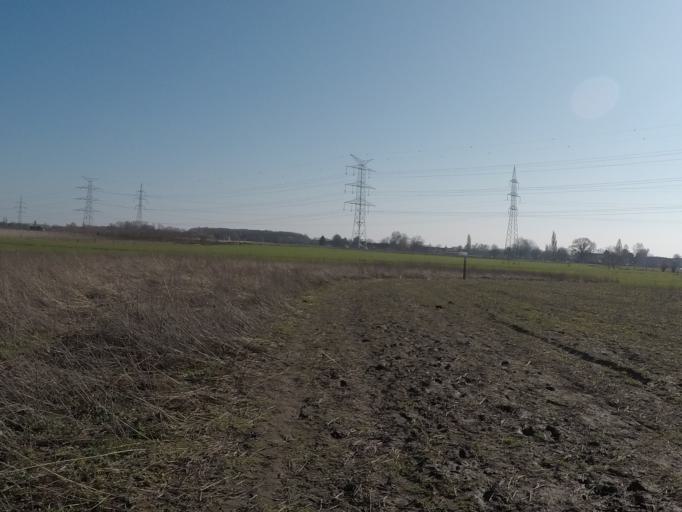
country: BE
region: Flanders
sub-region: Provincie Antwerpen
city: Aartselaar
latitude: 51.1189
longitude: 4.3787
